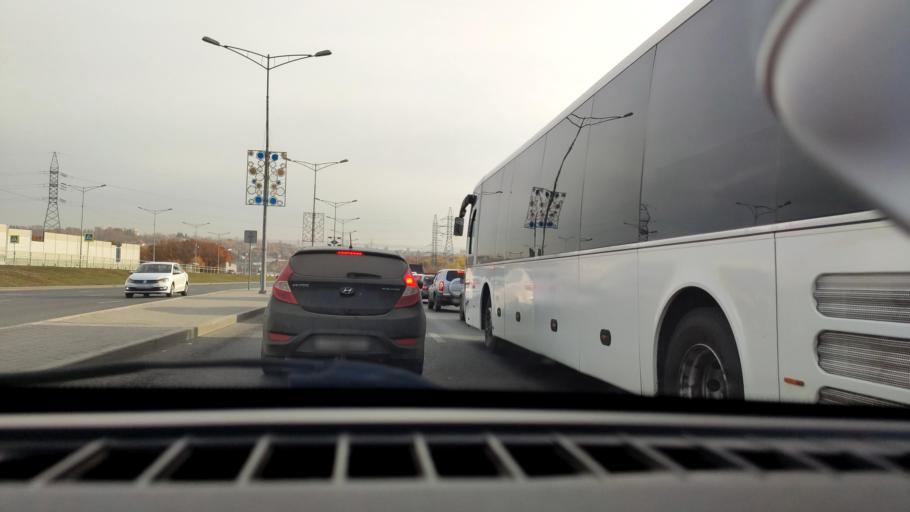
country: RU
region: Samara
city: Petra-Dubrava
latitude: 53.2782
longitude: 50.2725
